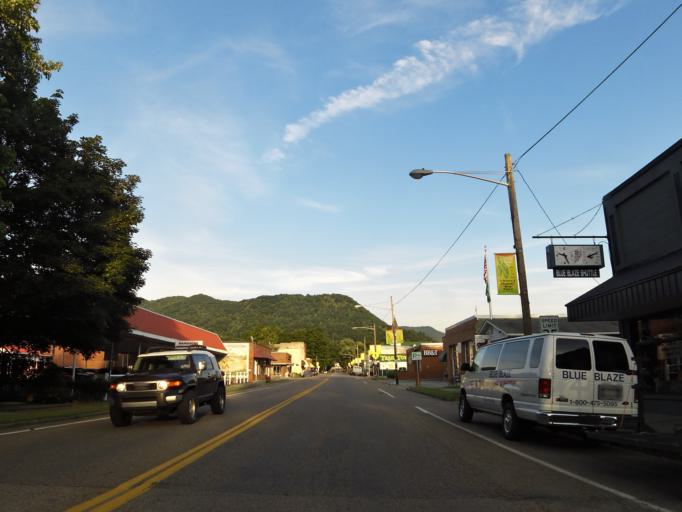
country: US
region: Virginia
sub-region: Washington County
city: Emory
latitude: 36.6355
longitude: -81.7909
